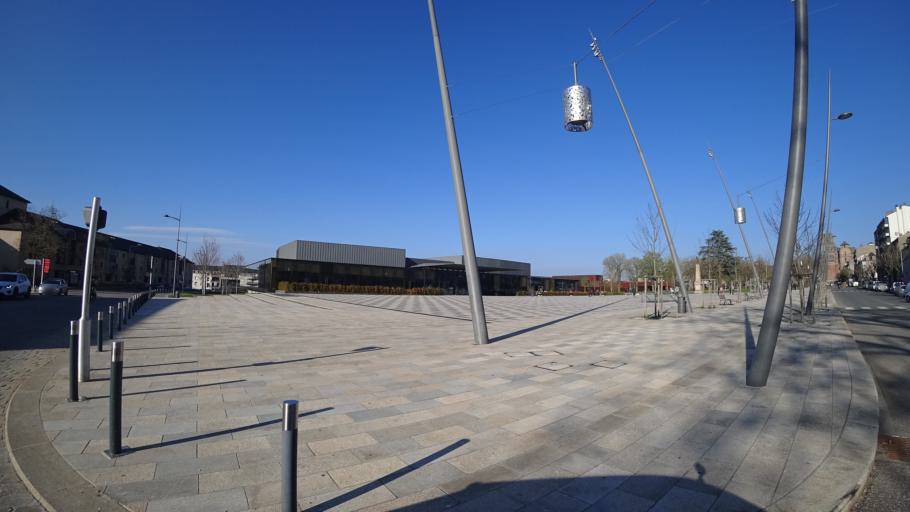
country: FR
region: Midi-Pyrenees
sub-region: Departement de l'Aveyron
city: Rodez
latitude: 44.3515
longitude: 2.5657
